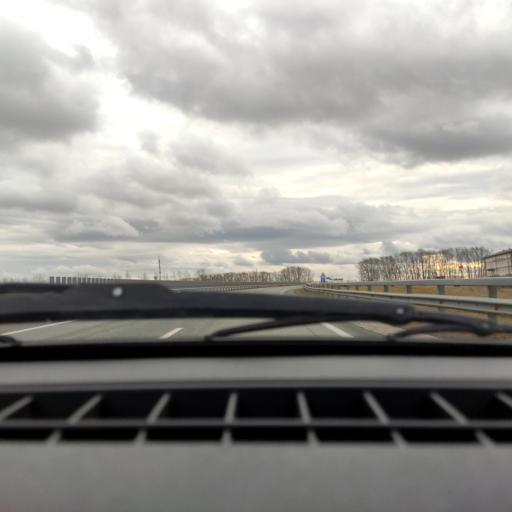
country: RU
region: Bashkortostan
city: Asanovo
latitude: 54.9633
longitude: 55.5831
